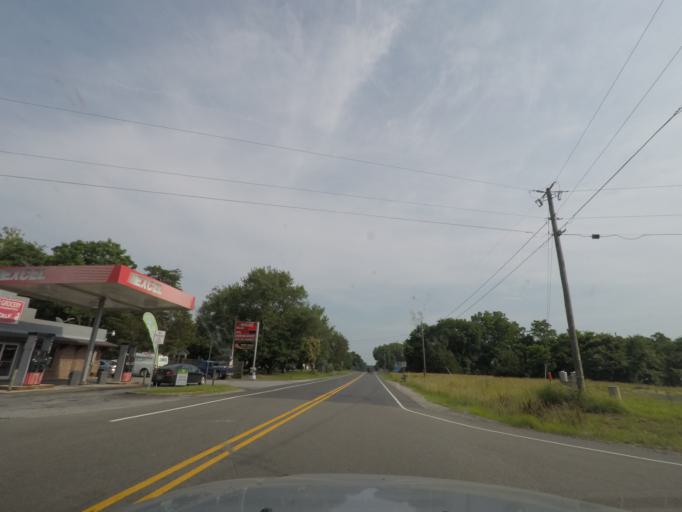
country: US
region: Virginia
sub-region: Prince Edward County
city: Hampden Sydney
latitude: 37.2301
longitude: -78.4428
